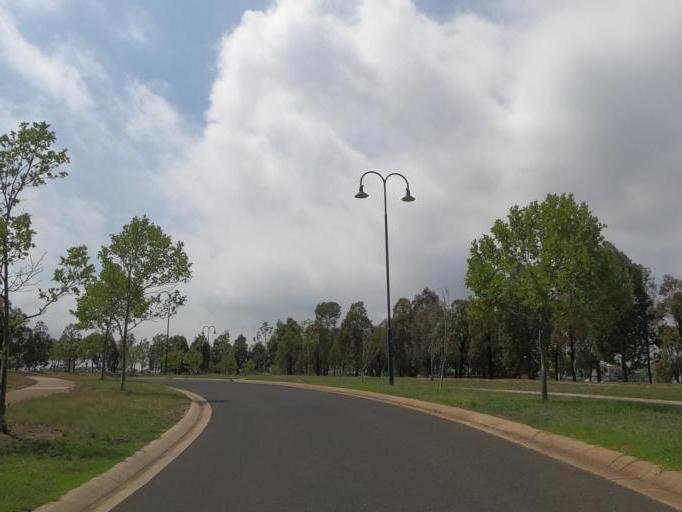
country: AU
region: Victoria
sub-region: Hume
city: Attwood
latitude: -37.6708
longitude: 144.8841
